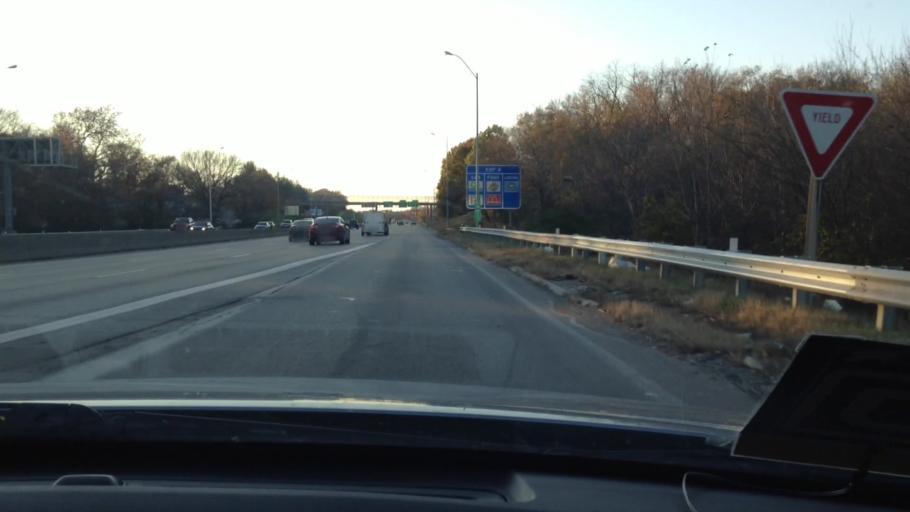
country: US
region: Missouri
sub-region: Jackson County
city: Kansas City
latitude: 39.0700
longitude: -94.5135
